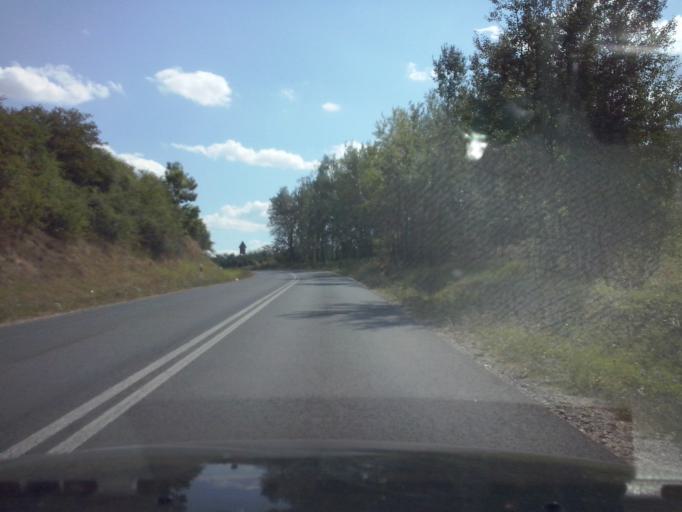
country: PL
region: Swietokrzyskie
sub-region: Powiat staszowski
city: Szydlow
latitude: 50.5870
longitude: 20.9628
